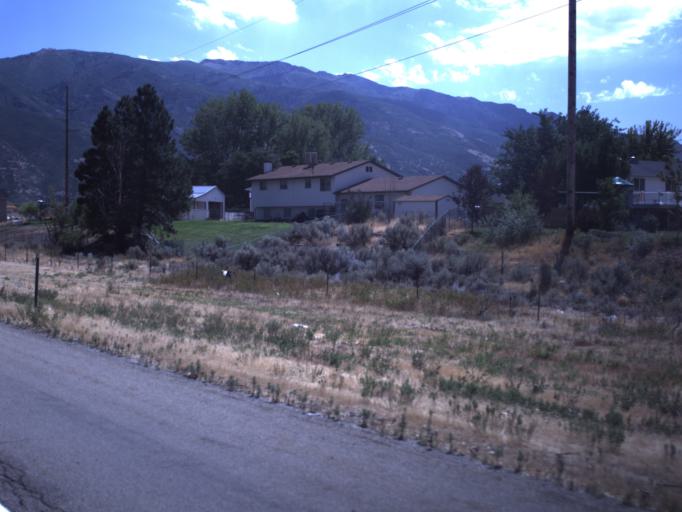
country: US
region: Utah
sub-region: Davis County
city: South Weber
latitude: 41.1368
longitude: -111.9397
